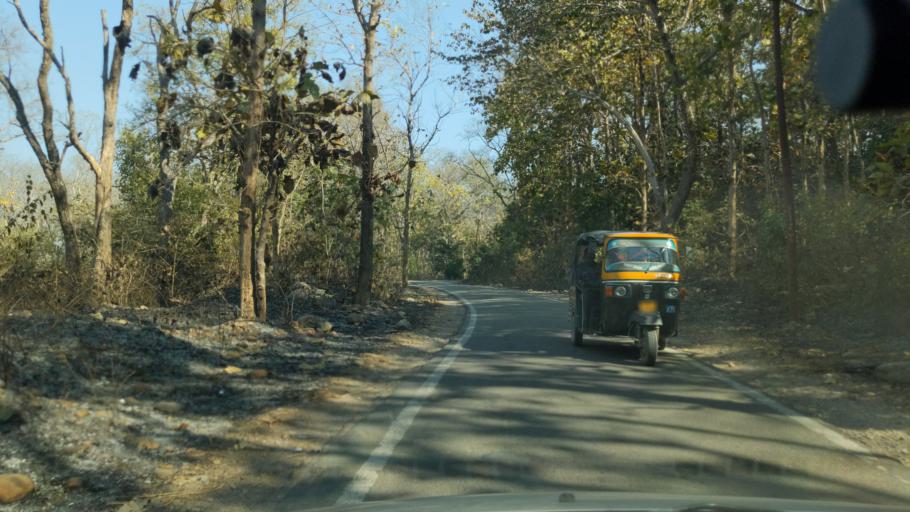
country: IN
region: Uttarakhand
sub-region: Naini Tal
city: Ramnagar
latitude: 29.4012
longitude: 79.1357
